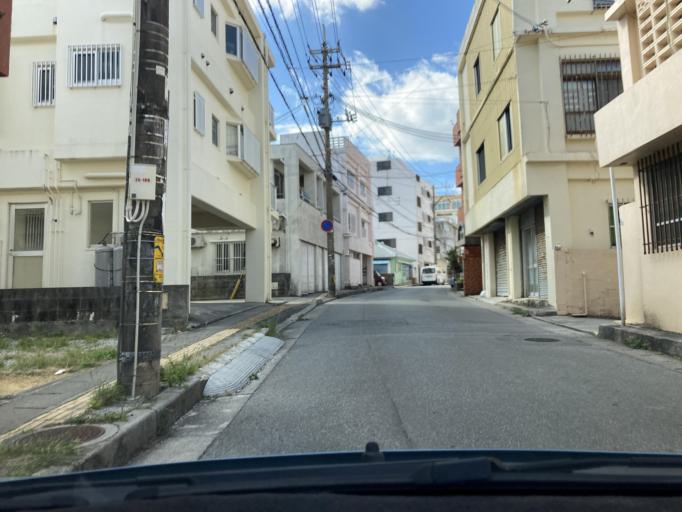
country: JP
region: Okinawa
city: Okinawa
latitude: 26.3319
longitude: 127.7983
